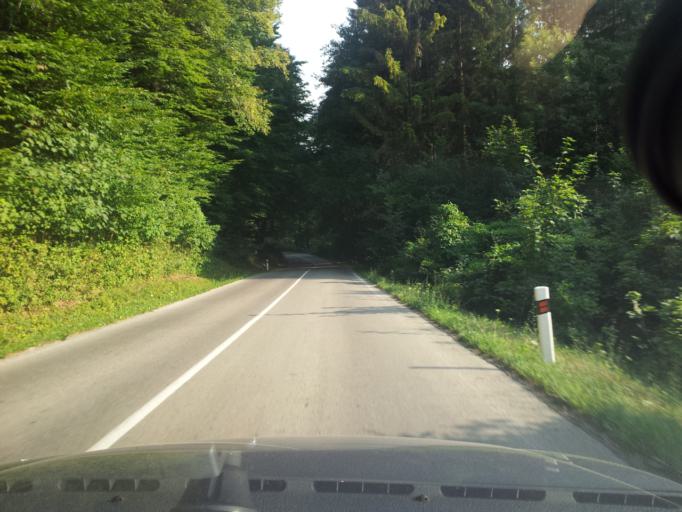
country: SK
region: Nitriansky
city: Trencianske Teplice
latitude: 48.8805
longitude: 18.1862
